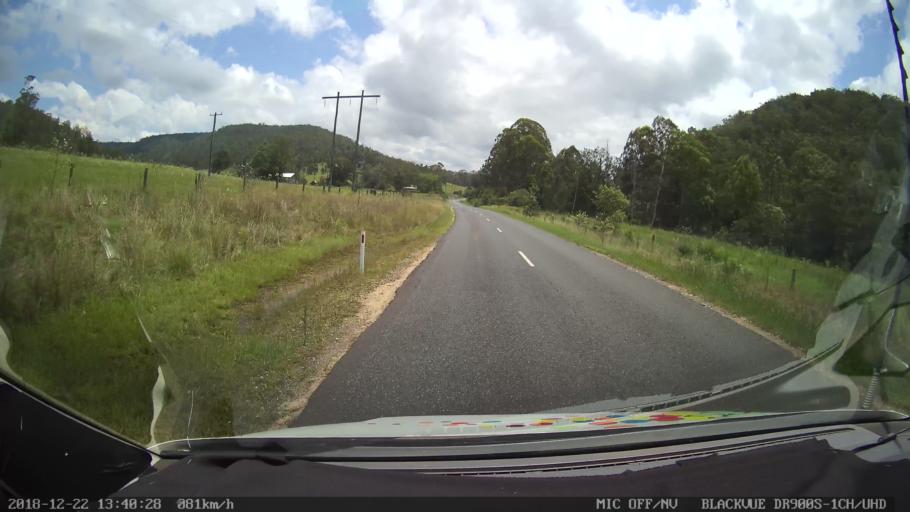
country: AU
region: New South Wales
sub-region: Clarence Valley
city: Coutts Crossing
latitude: -29.9184
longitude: 152.7766
